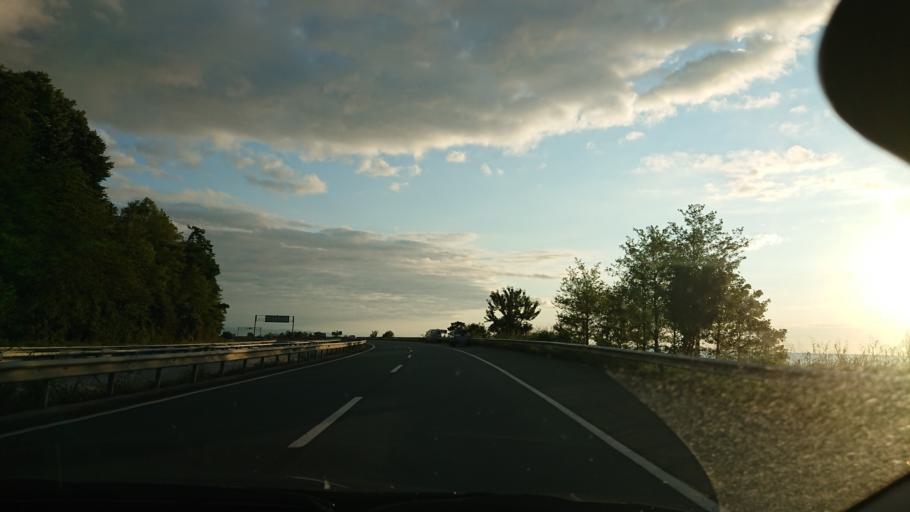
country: TR
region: Rize
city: Pazar
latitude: 41.1611
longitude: 40.8033
